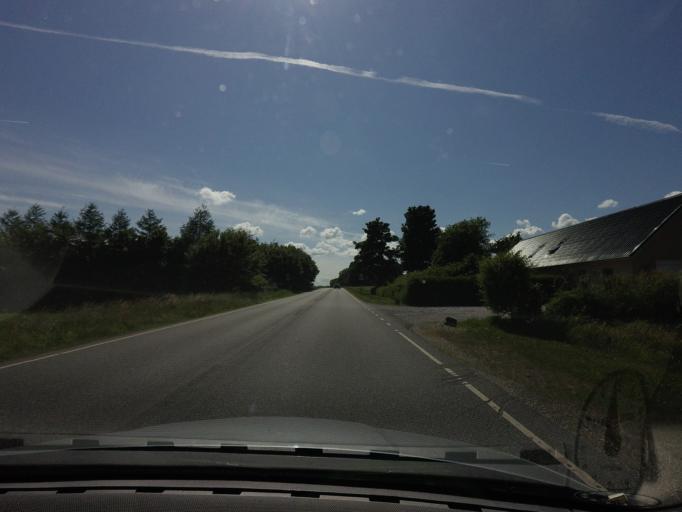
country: DK
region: Central Jutland
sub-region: Norddjurs Kommune
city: Grenaa
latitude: 56.3409
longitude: 10.7490
